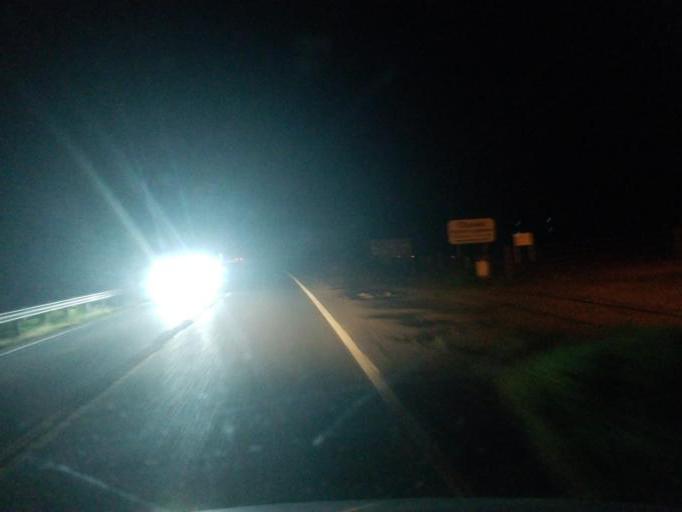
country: US
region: Ohio
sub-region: Stark County
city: Minerva
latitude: 40.7417
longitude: -81.0008
